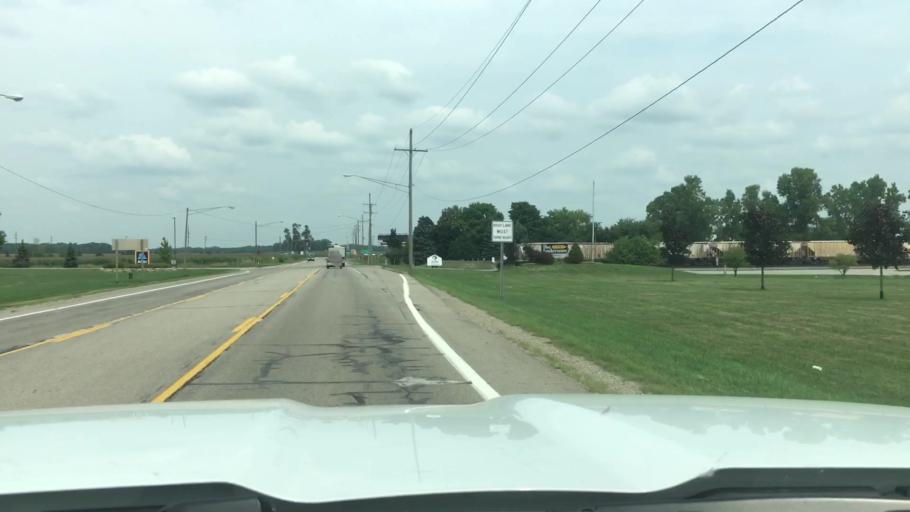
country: US
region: Michigan
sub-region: Ingham County
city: Webberville
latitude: 42.6645
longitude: -84.1984
